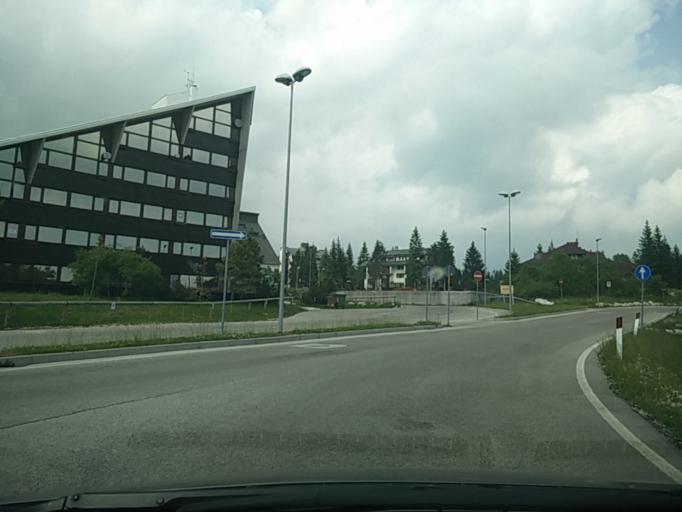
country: IT
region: Friuli Venezia Giulia
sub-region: Provincia di Pordenone
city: Budoia
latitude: 46.1076
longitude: 12.5198
